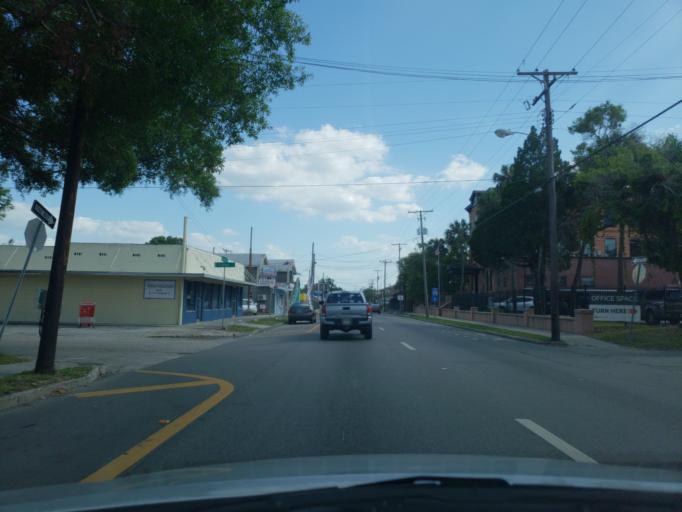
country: US
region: Florida
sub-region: Hillsborough County
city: Tampa
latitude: 27.9683
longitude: -82.4849
